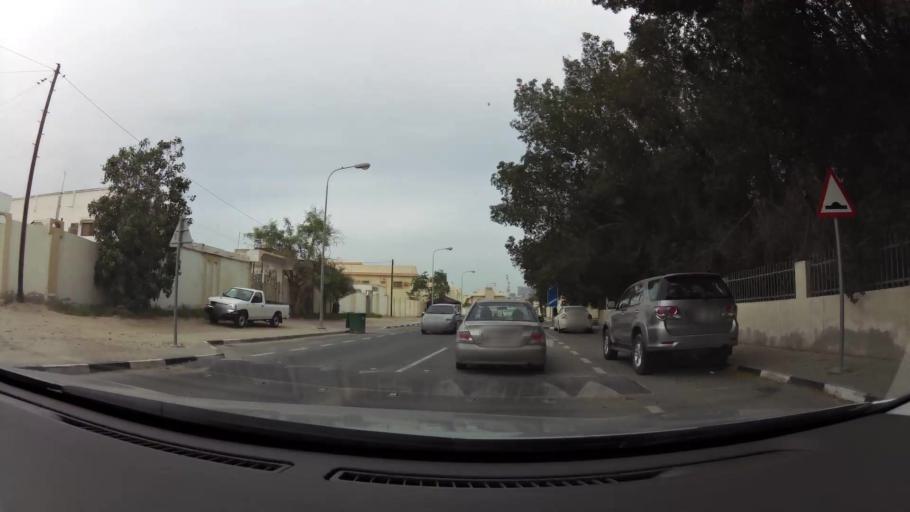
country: QA
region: Baladiyat ad Dawhah
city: Doha
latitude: 25.3107
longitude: 51.4901
